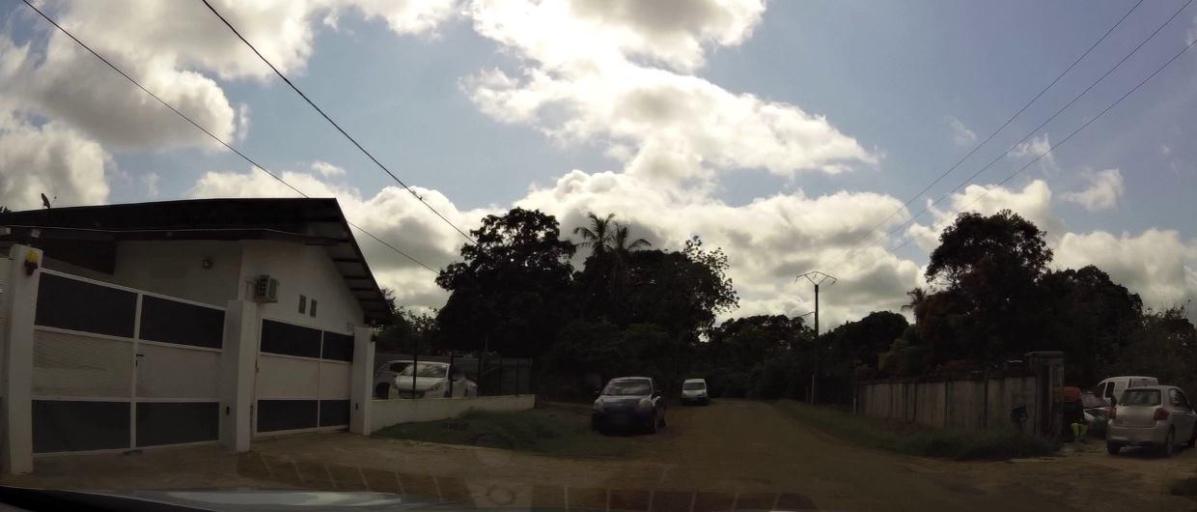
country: GF
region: Guyane
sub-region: Guyane
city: Matoury
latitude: 4.8320
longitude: -52.3088
